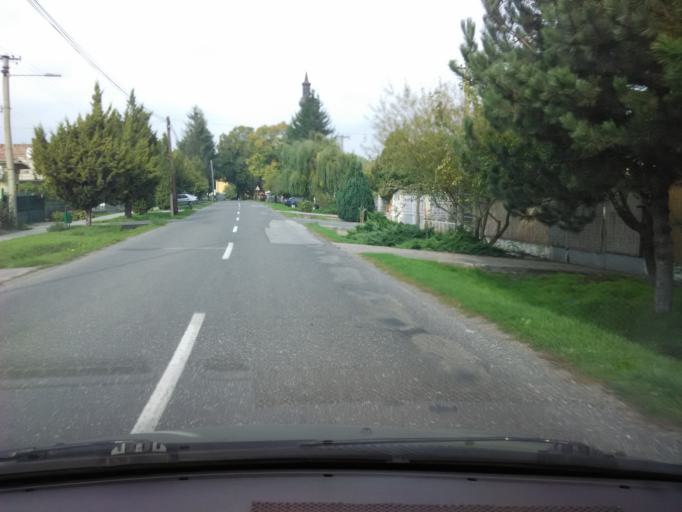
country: SK
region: Nitriansky
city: Tlmace
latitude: 48.2419
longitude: 18.5210
